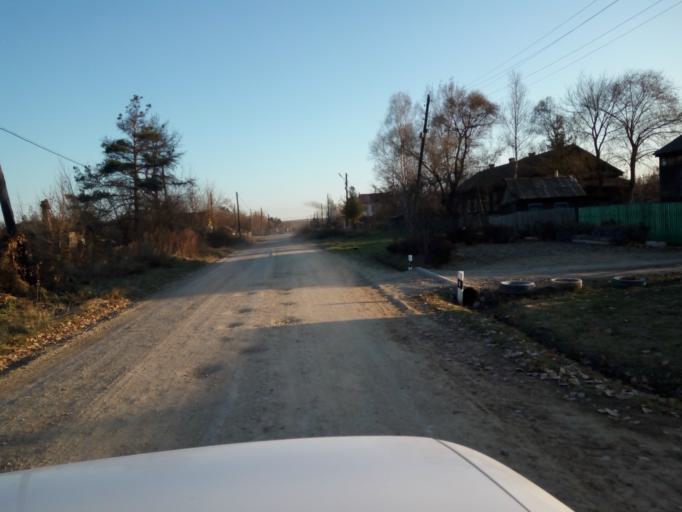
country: RU
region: Primorskiy
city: Lazo
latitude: 45.8771
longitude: 133.6509
